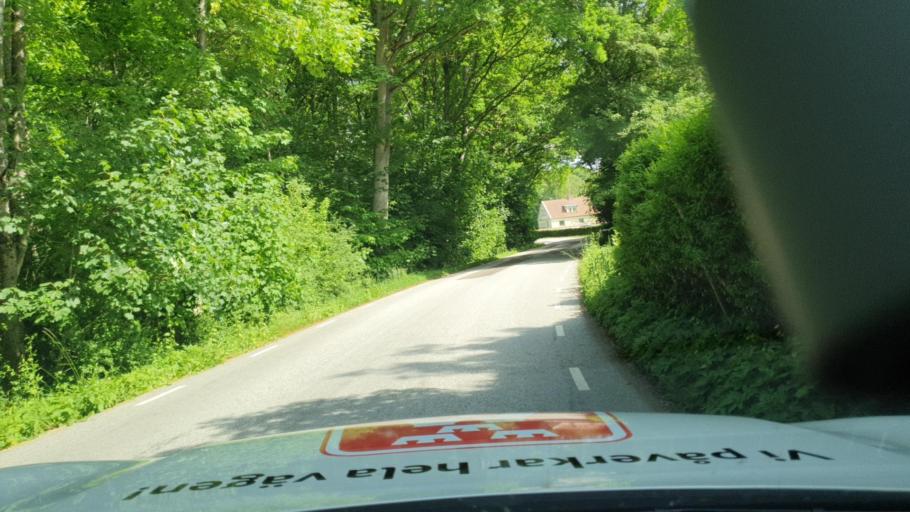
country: SE
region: Skane
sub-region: Svedala Kommun
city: Svedala
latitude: 55.5268
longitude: 13.2895
